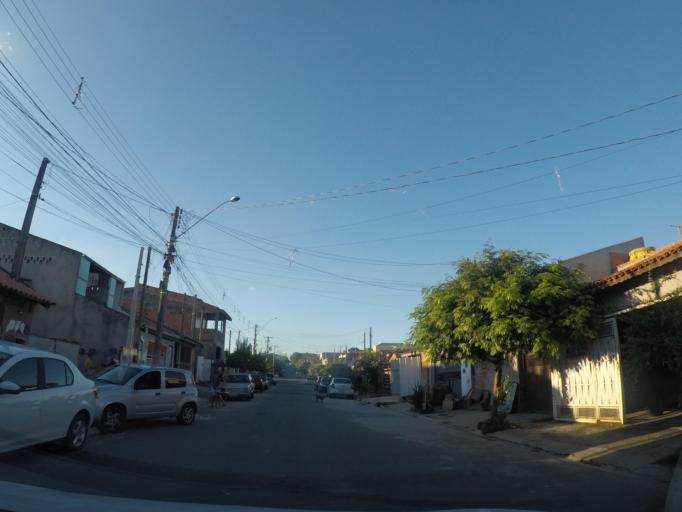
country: BR
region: Sao Paulo
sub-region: Sumare
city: Sumare
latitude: -22.8329
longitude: -47.2441
